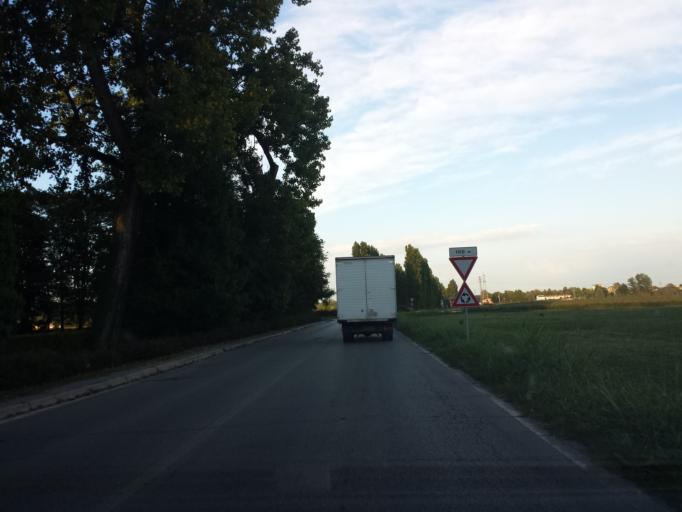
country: IT
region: Veneto
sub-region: Provincia di Vicenza
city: Creazzo
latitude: 45.5471
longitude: 11.4911
